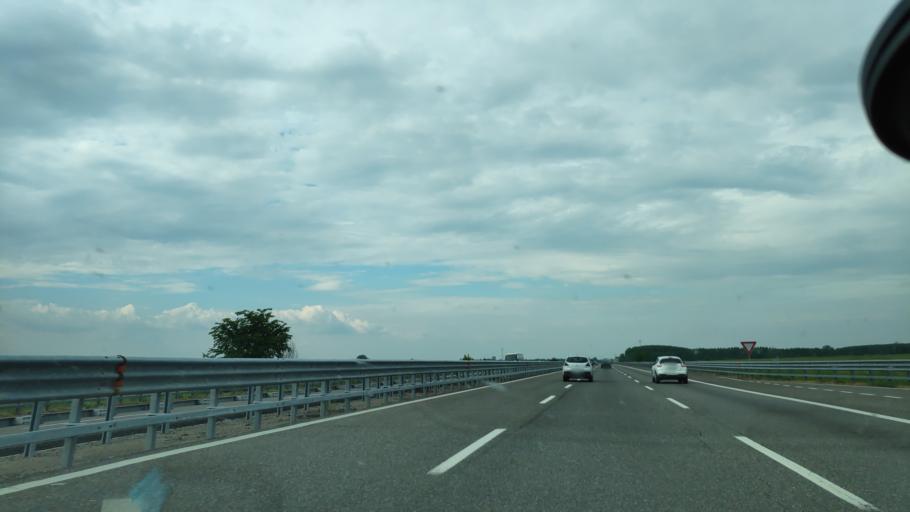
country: IT
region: Lombardy
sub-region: Provincia di Pavia
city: Silvano Pietra
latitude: 45.0484
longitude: 8.9485
